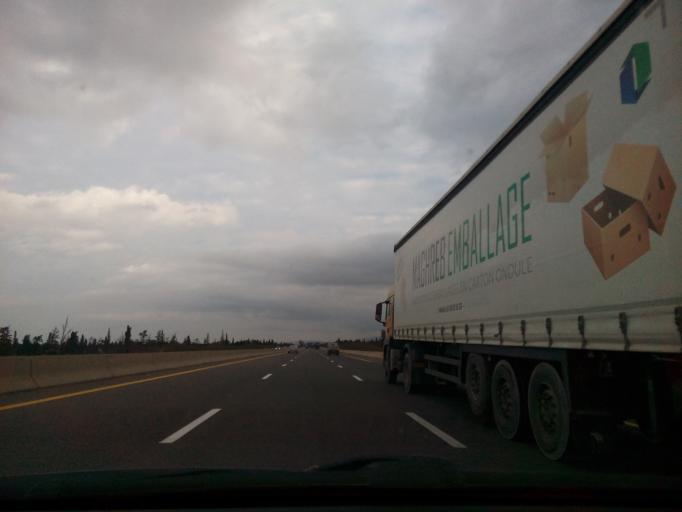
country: DZ
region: Mascara
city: Sig
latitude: 35.6167
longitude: 0.0170
